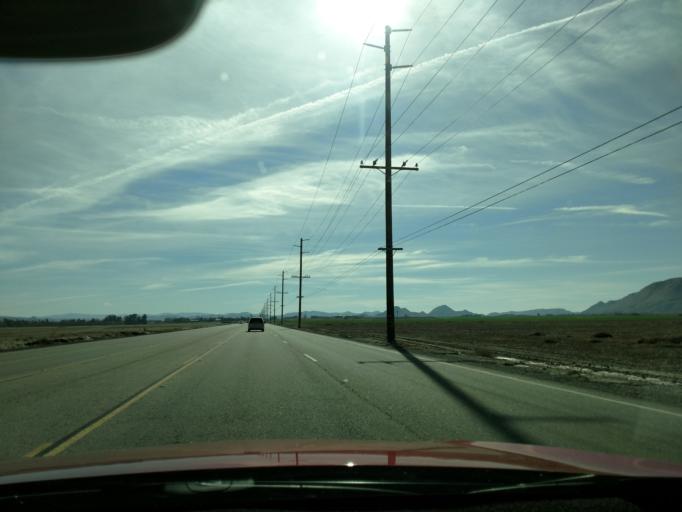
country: US
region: California
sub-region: Riverside County
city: San Jacinto
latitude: 33.8155
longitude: -117.0071
